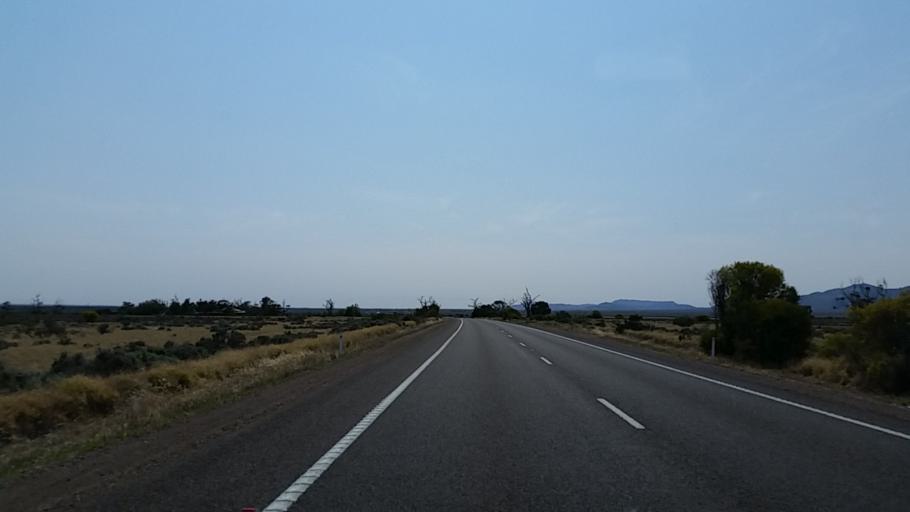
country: AU
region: South Australia
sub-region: Port Augusta
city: Port Augusta
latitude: -32.6933
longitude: 137.9416
